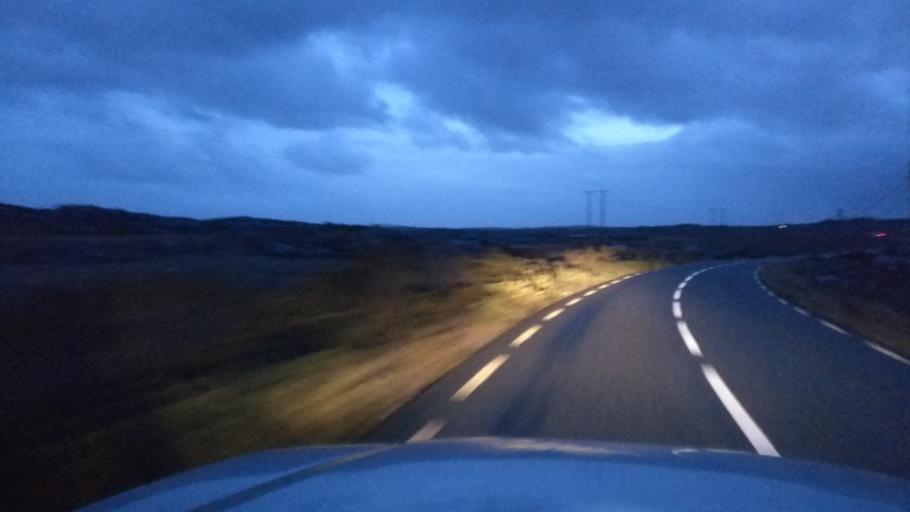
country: IE
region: Connaught
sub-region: County Galway
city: Oughterard
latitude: 53.4050
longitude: -9.5420
